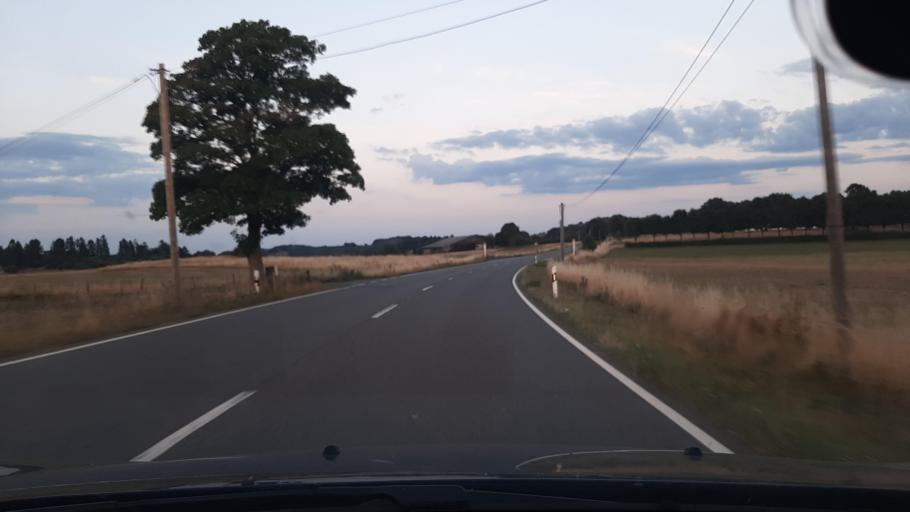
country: DE
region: North Rhine-Westphalia
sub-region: Regierungsbezirk Koln
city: Nettersheim
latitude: 50.5206
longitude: 6.6305
